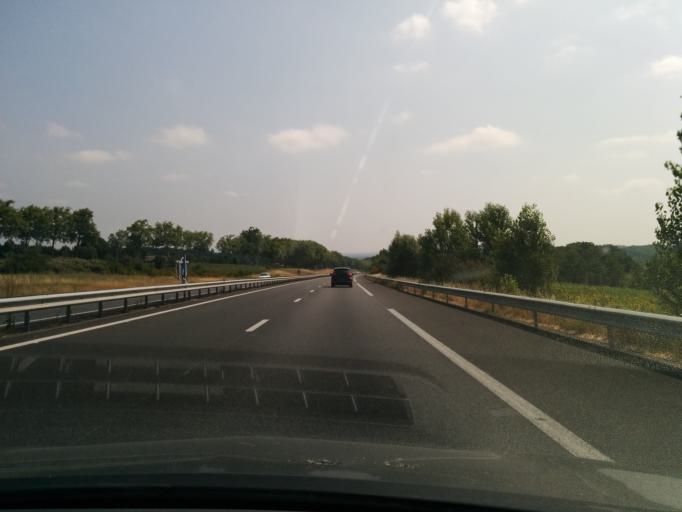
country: FR
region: Midi-Pyrenees
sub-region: Departement de la Haute-Garonne
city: Montastruc-la-Conseillere
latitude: 43.7409
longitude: 1.5924
